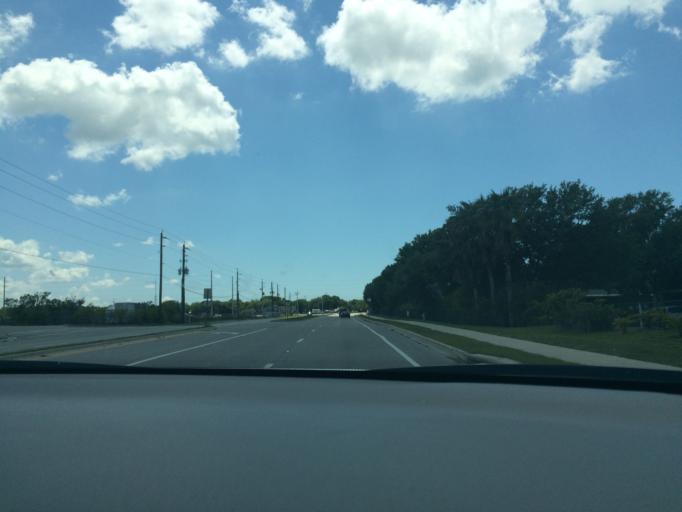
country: US
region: Florida
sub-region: Manatee County
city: Samoset
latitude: 27.4496
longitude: -82.4852
